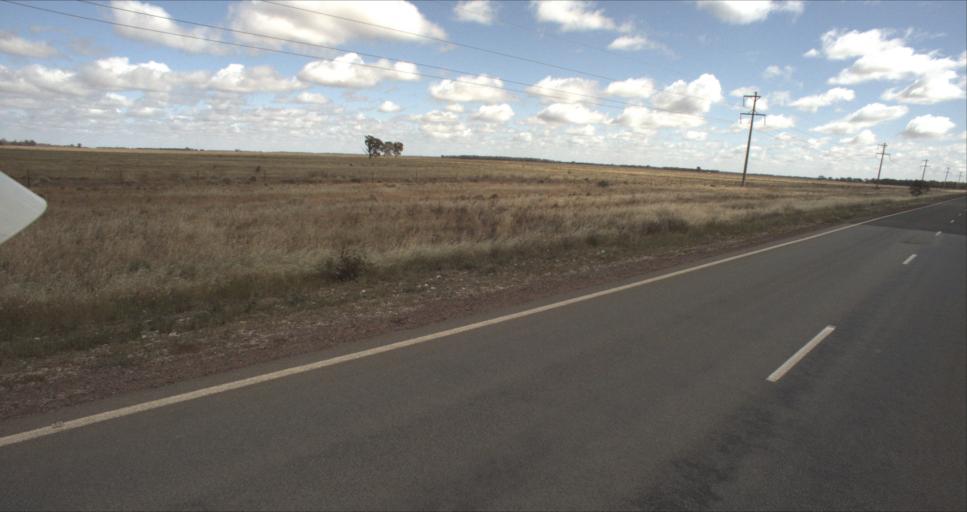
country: AU
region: New South Wales
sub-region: Murrumbidgee Shire
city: Darlington Point
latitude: -34.5905
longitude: 146.1636
